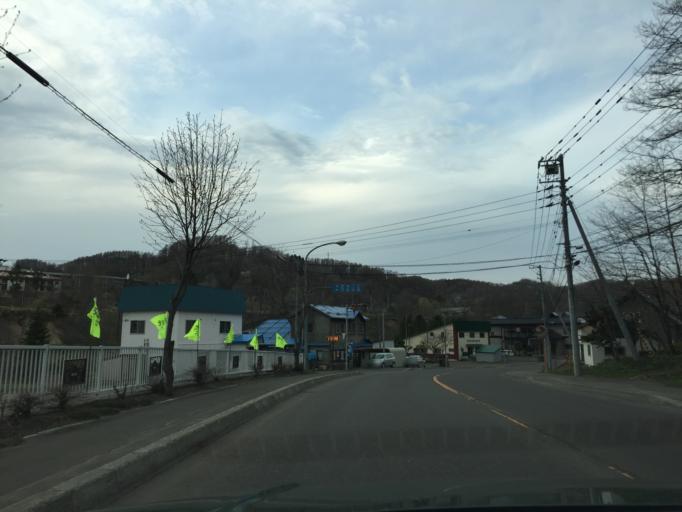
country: JP
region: Hokkaido
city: Utashinai
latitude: 43.5156
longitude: 142.0269
